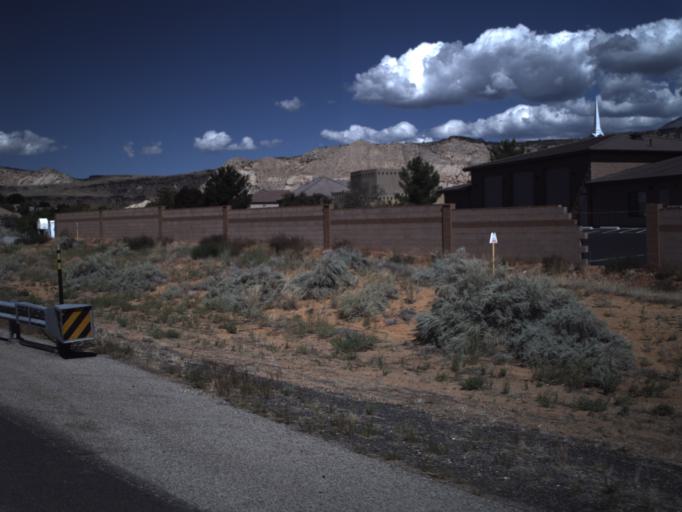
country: US
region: Utah
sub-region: Washington County
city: Ivins
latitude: 37.2002
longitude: -113.6251
